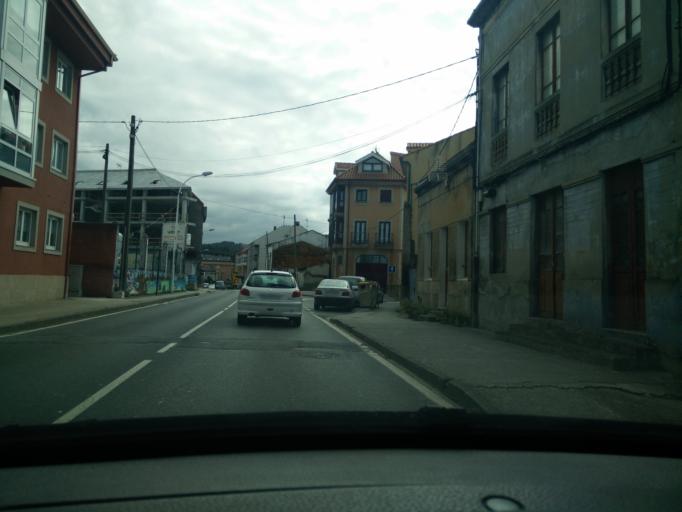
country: ES
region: Galicia
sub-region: Provincia da Coruna
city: A Coruna
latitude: 43.3327
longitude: -8.4247
